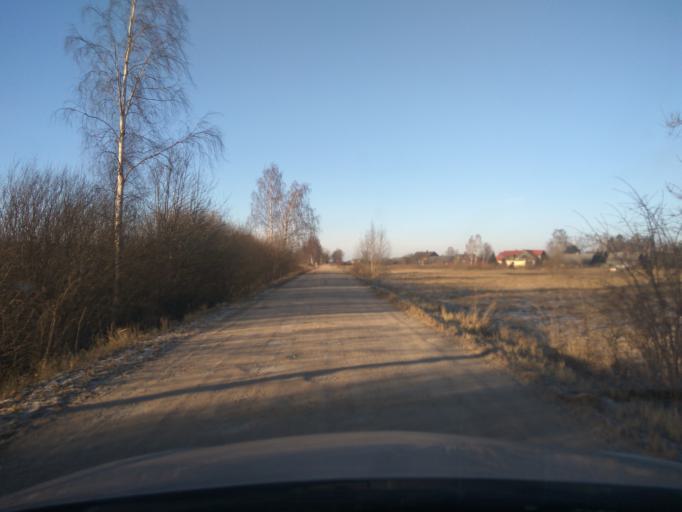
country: LV
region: Kuldigas Rajons
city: Kuldiga
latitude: 56.9687
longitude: 21.9421
